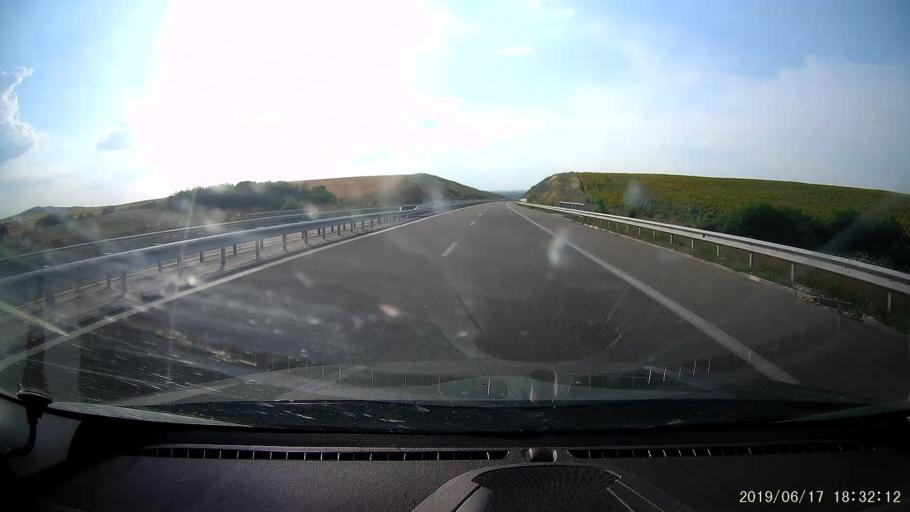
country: BG
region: Khaskovo
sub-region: Obshtina Dimitrovgrad
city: Dimitrovgrad
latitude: 42.0561
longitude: 25.4847
